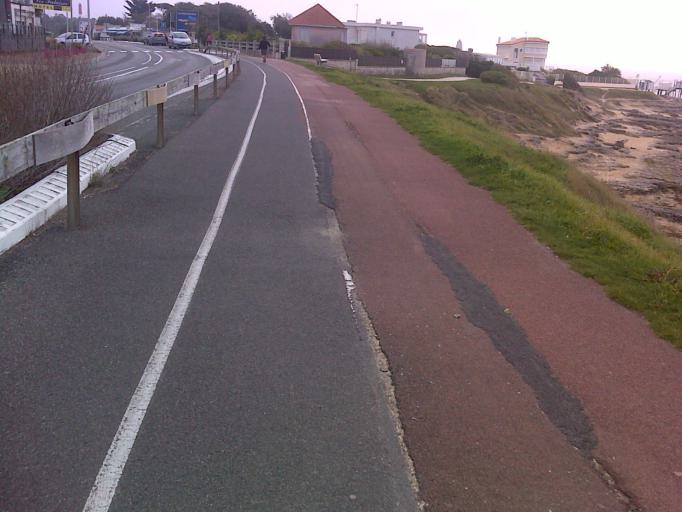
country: FR
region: Poitou-Charentes
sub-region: Departement de la Charente-Maritime
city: Saint-Palais-sur-Mer
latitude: 45.6487
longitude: -1.1165
